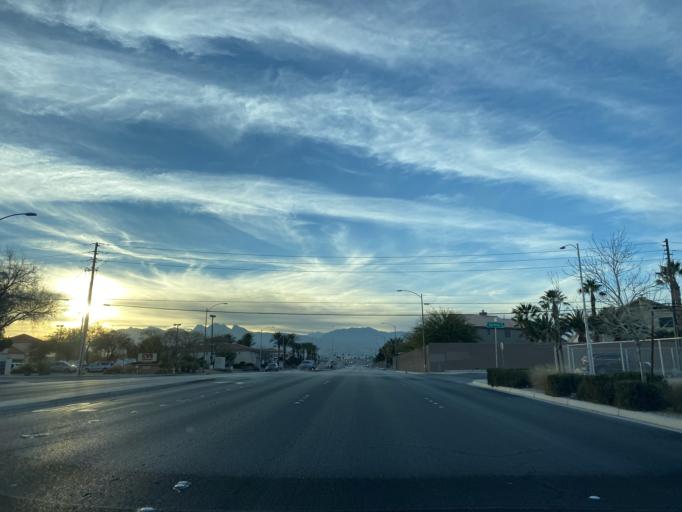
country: US
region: Nevada
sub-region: Clark County
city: Las Vegas
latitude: 36.2632
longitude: -115.2465
